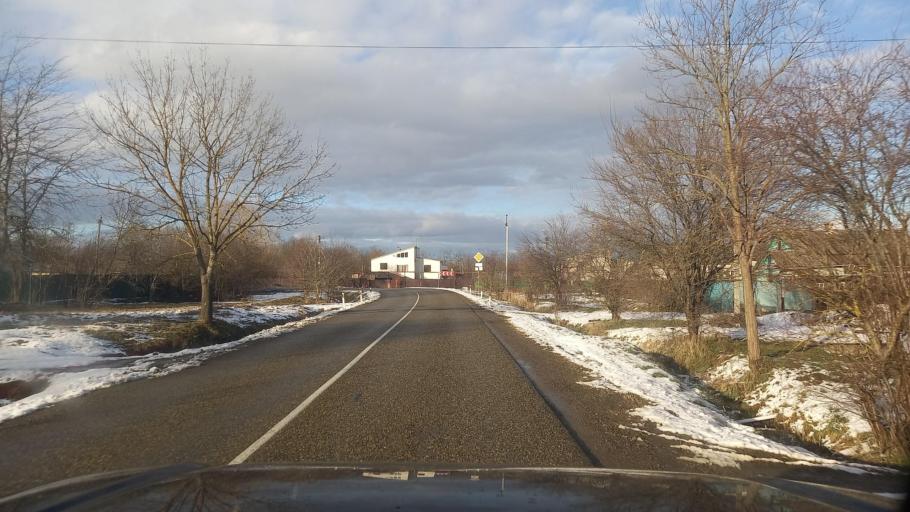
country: RU
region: Krasnodarskiy
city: Smolenskaya
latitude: 44.7754
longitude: 38.8460
